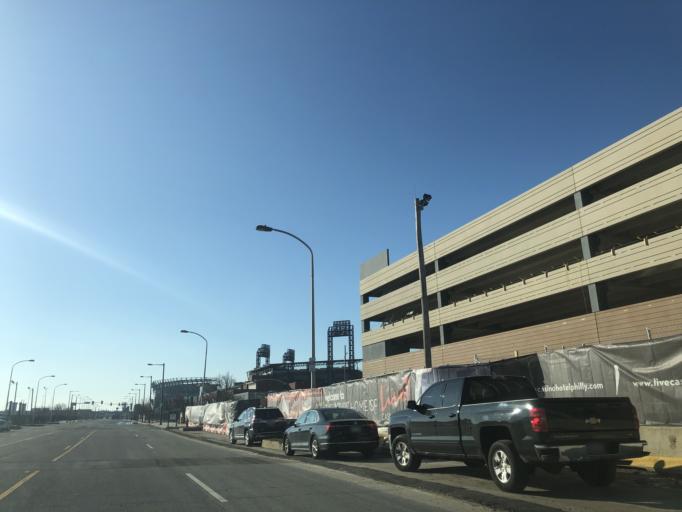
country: US
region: Pennsylvania
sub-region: Philadelphia County
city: Philadelphia
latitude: 39.9089
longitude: -75.1637
